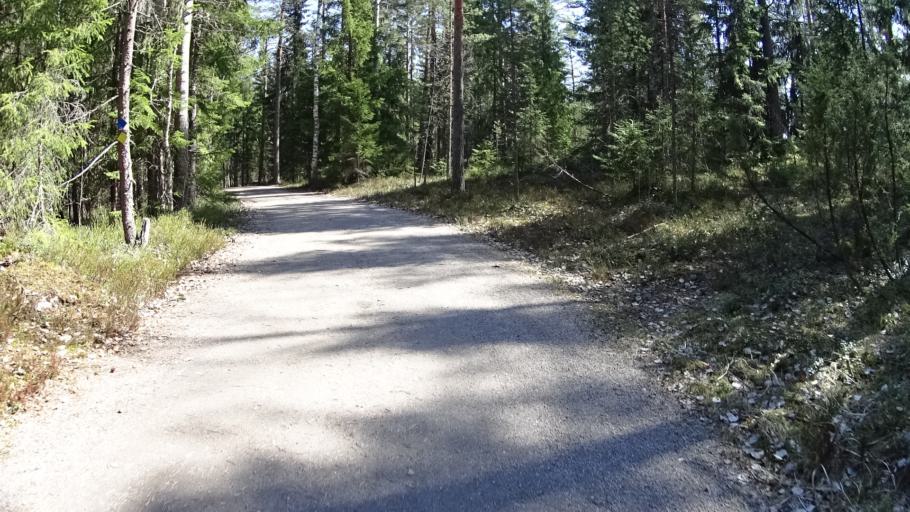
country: FI
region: Uusimaa
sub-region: Helsinki
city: Espoo
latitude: 60.2718
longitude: 24.6270
